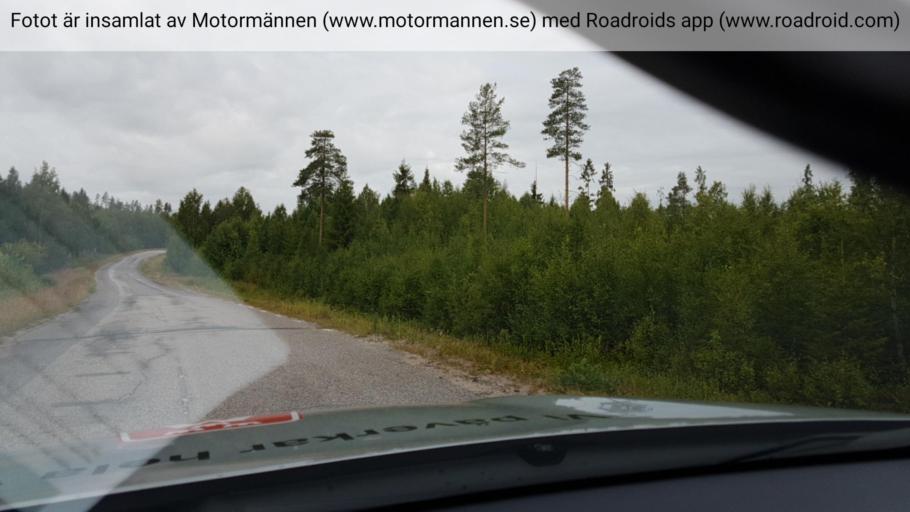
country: SE
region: Norrbotten
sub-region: Bodens Kommun
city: Saevast
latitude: 65.6677
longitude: 21.7639
